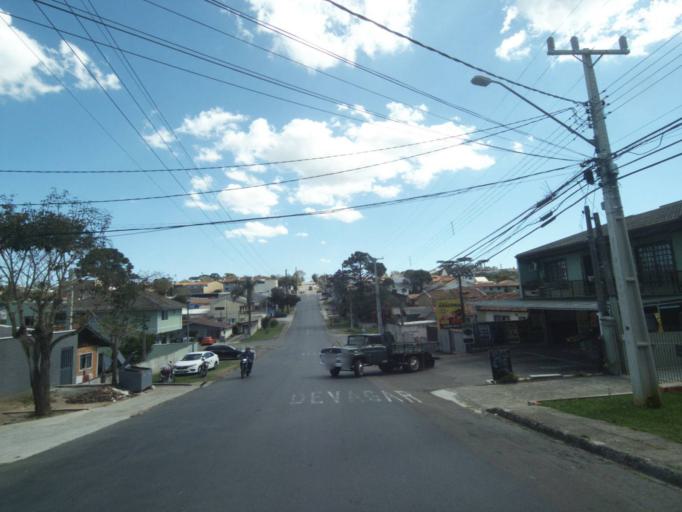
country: BR
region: Parana
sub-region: Curitiba
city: Curitiba
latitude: -25.3781
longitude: -49.2540
